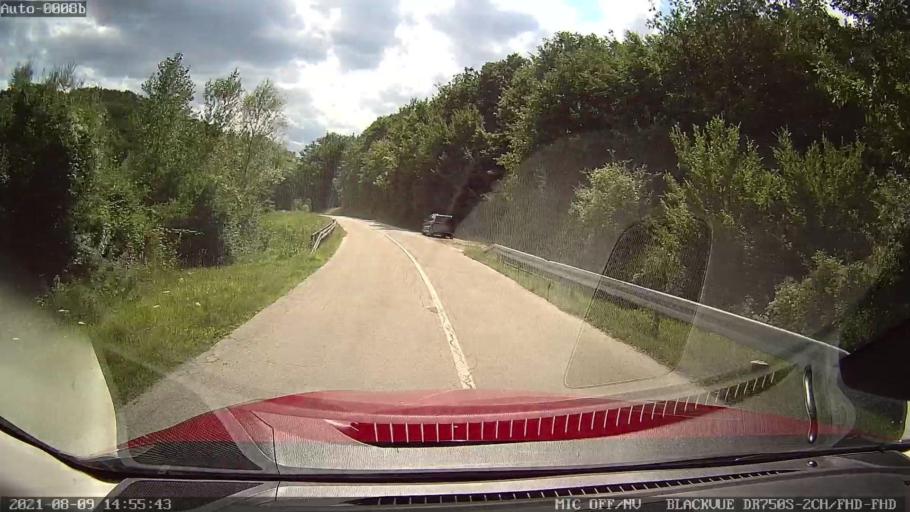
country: HR
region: Istarska
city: Pazin
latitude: 45.2744
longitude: 14.0636
